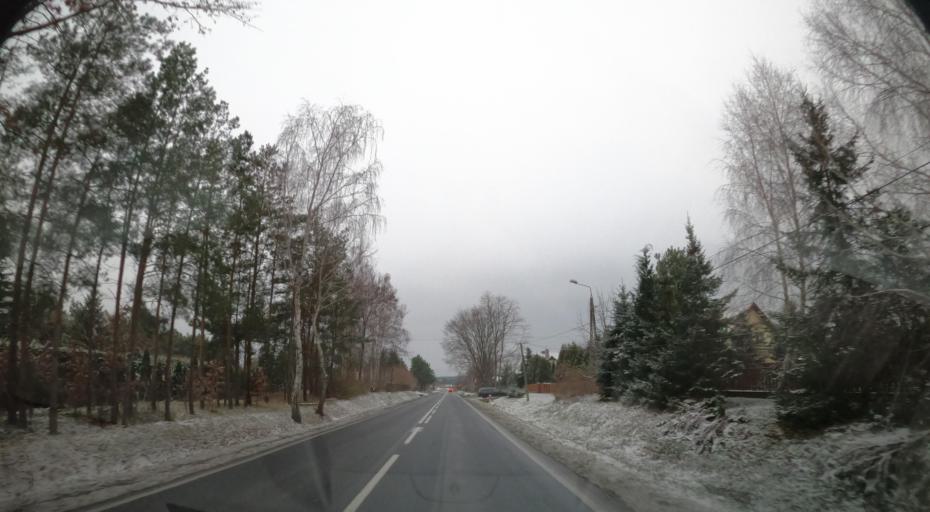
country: PL
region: Masovian Voivodeship
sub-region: Powiat plocki
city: Maszewo Duze
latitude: 52.5719
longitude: 19.5941
